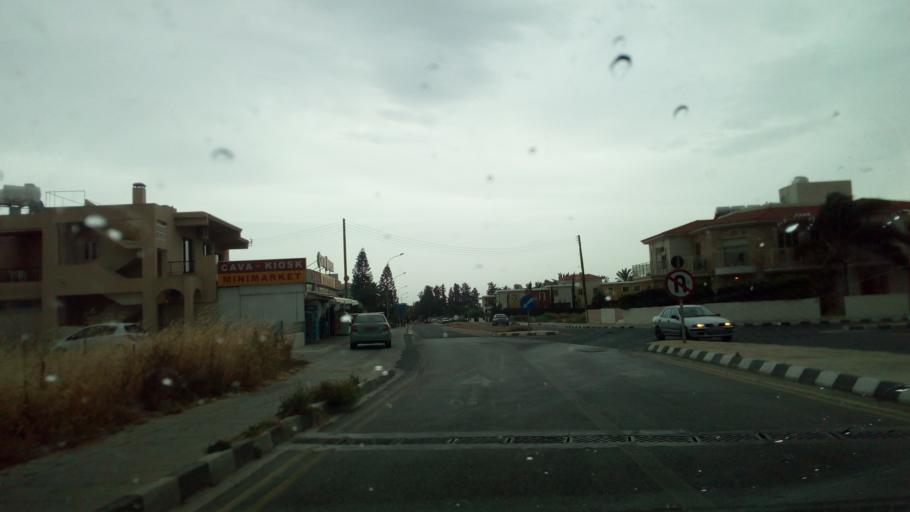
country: CY
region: Pafos
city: Paphos
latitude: 34.7618
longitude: 32.4237
